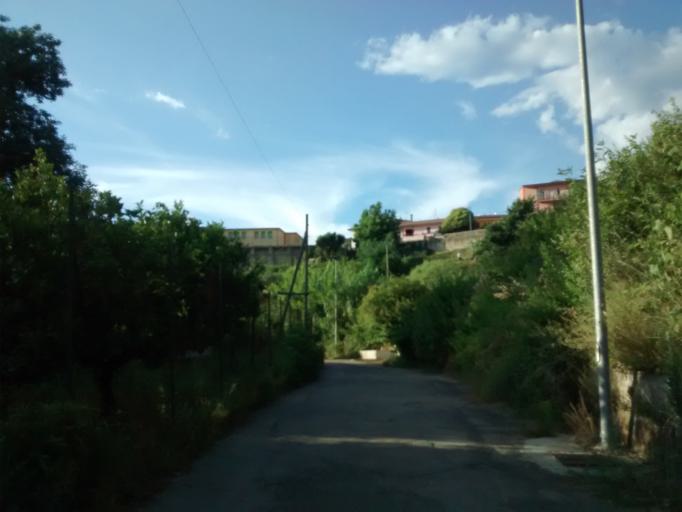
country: IT
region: Calabria
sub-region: Provincia di Catanzaro
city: Cortale
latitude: 38.8863
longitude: 16.4077
